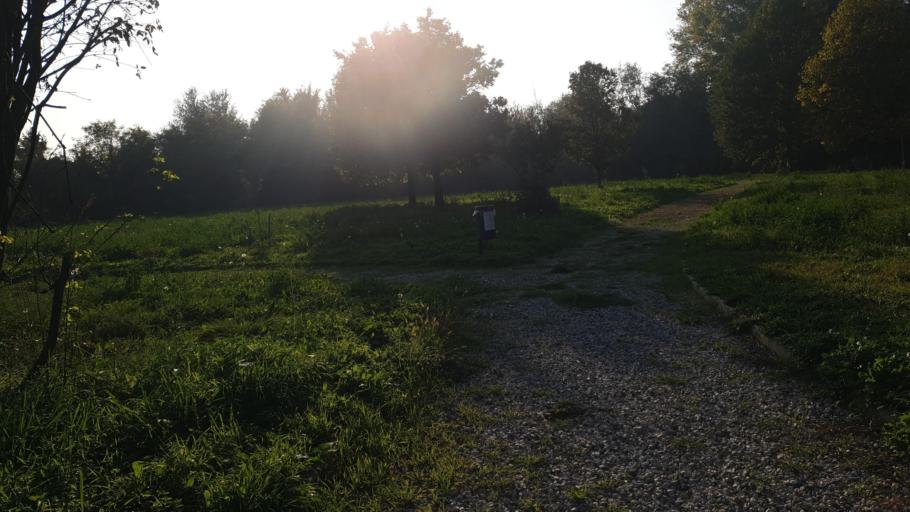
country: IT
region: Veneto
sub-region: Provincia di Padova
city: Ponte San Nicolo
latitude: 45.3791
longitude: 11.9431
